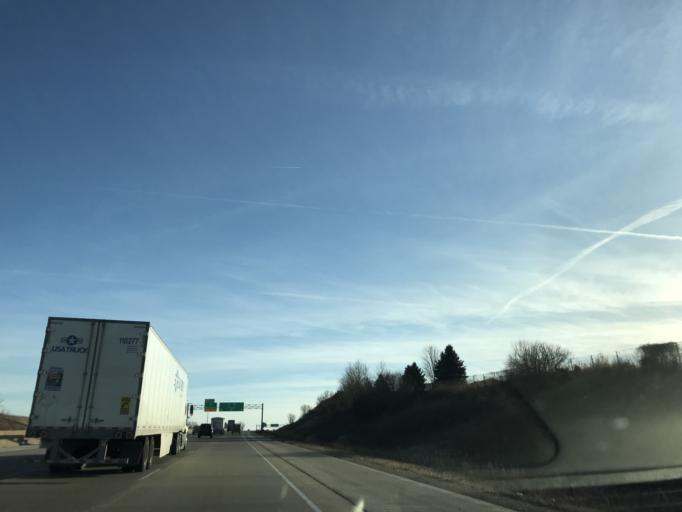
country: US
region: Wisconsin
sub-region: Dane County
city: Monona
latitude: 43.1154
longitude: -89.2873
